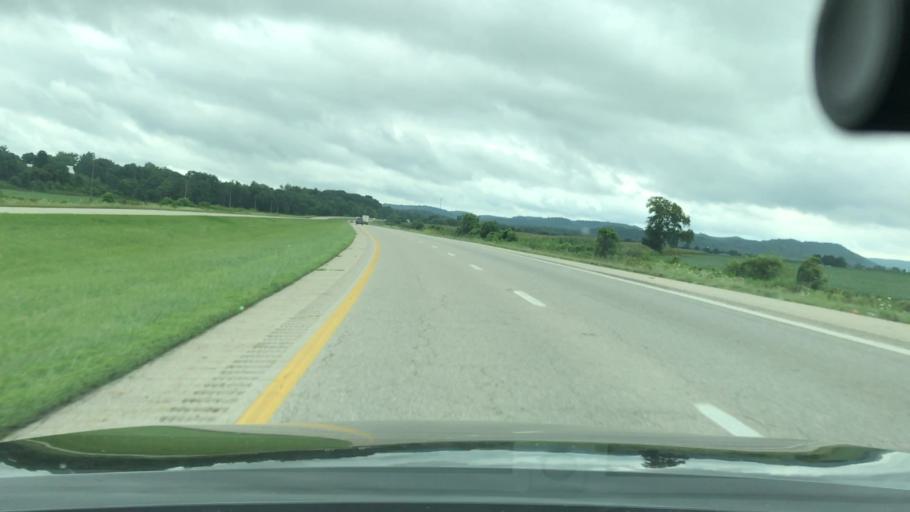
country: US
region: Ohio
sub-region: Ross County
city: Chillicothe
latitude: 39.2702
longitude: -82.8816
